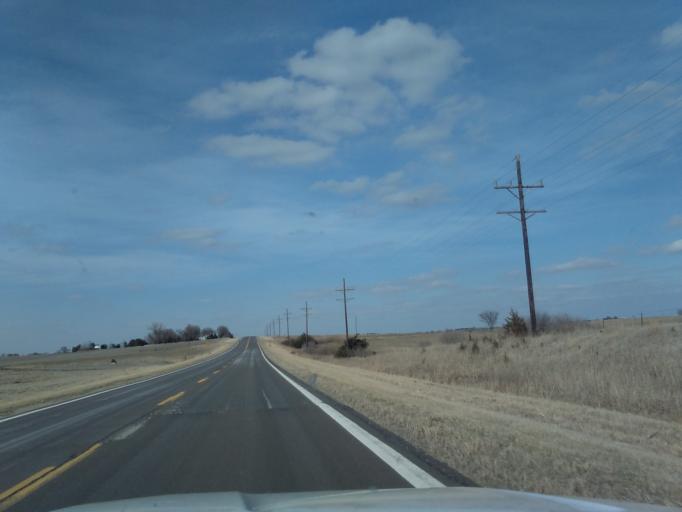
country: US
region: Nebraska
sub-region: Gage County
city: Beatrice
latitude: 40.1441
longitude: -96.9352
